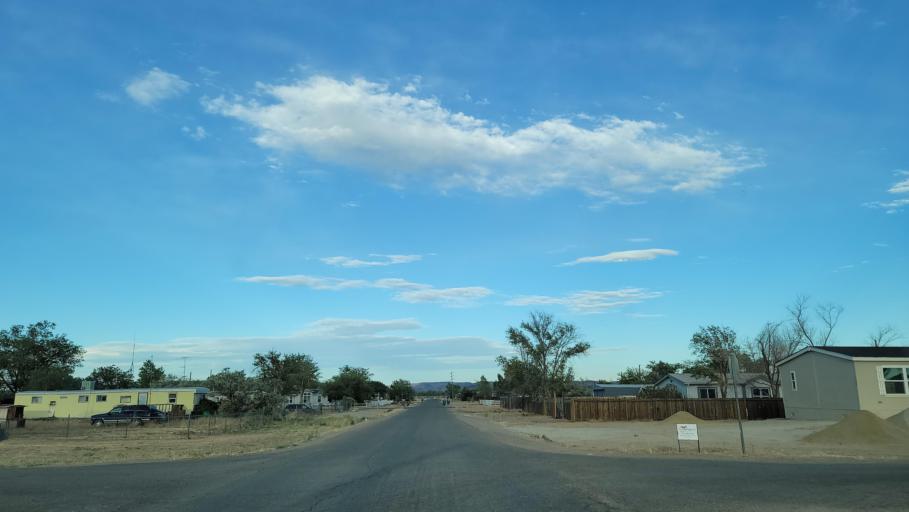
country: US
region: Nevada
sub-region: Lyon County
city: Silver Springs
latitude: 39.4128
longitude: -119.2228
